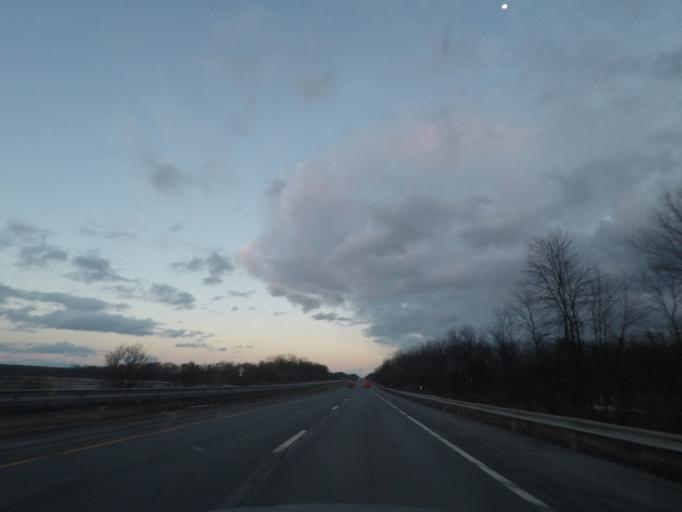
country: US
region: New York
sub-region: Montgomery County
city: Tribes Hill
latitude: 42.9304
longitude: -74.2966
